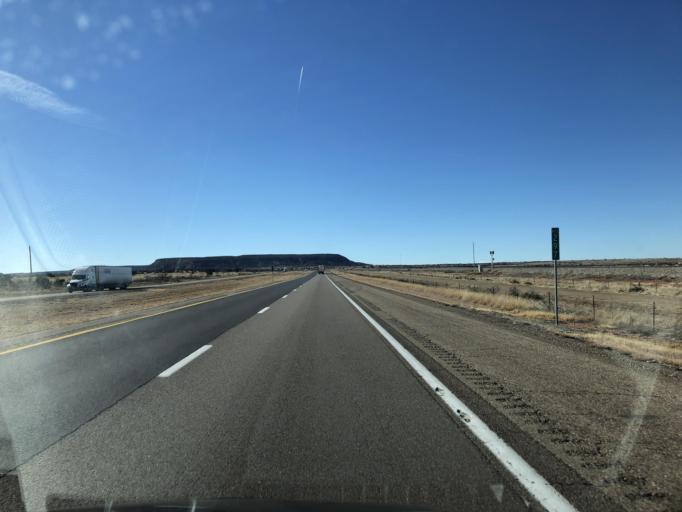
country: US
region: New Mexico
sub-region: Guadalupe County
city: Santa Rosa
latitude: 35.0570
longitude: -104.3209
